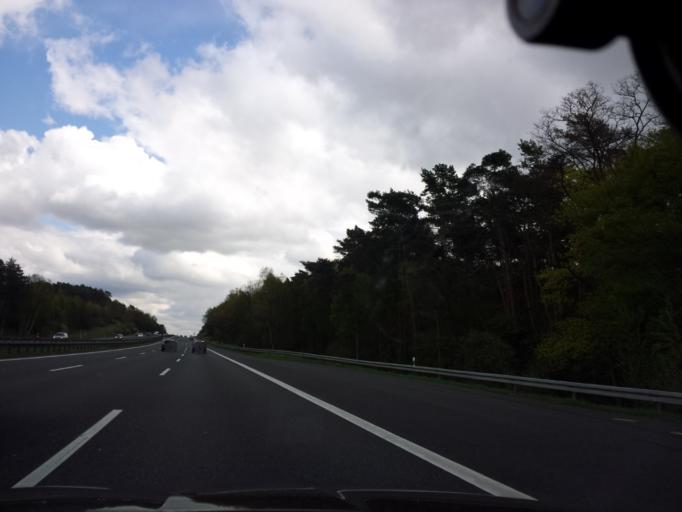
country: DE
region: Brandenburg
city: Rangsdorf
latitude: 52.3061
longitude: 13.3971
